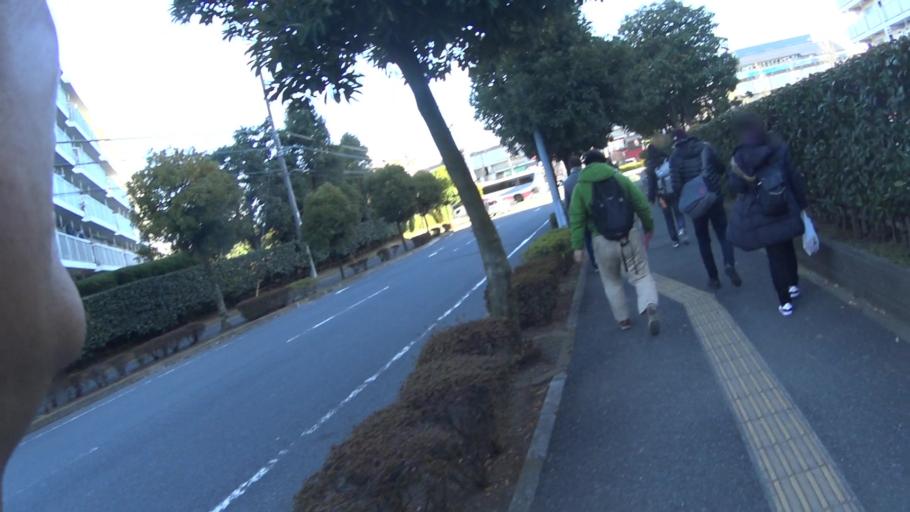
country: JP
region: Tokyo
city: Urayasu
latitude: 35.6441
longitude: 139.9044
